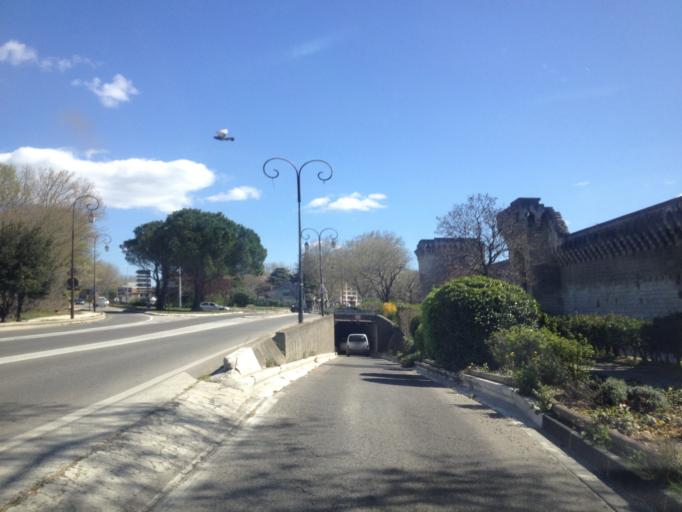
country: FR
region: Provence-Alpes-Cote d'Azur
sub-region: Departement du Vaucluse
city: Avignon
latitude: 43.9529
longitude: 4.8153
